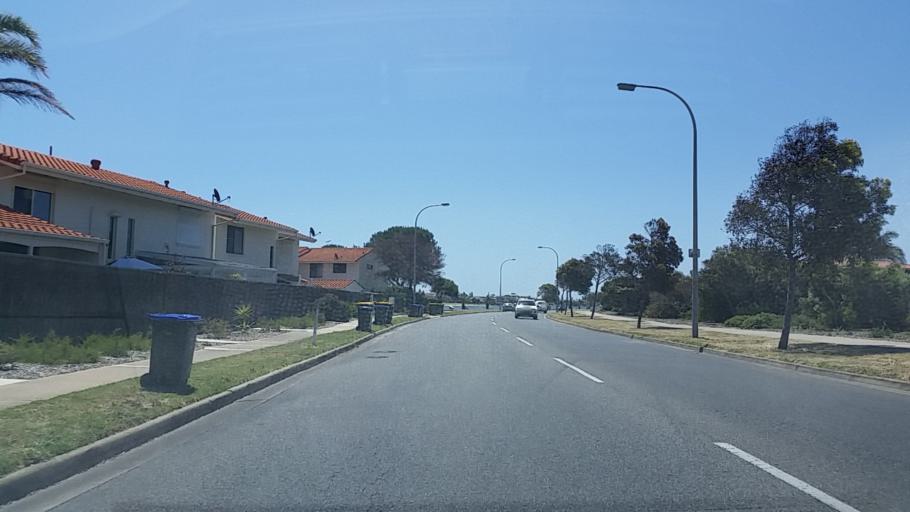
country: AU
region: South Australia
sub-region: Charles Sturt
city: Grange
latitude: -34.8912
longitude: 138.4913
